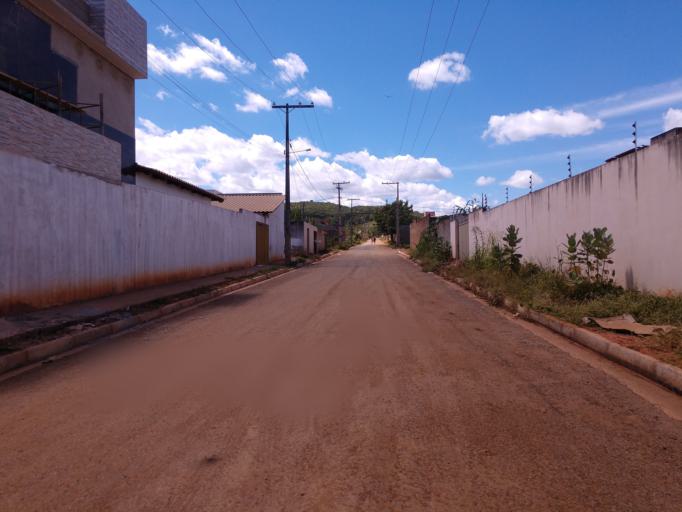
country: BR
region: Bahia
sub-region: Sao Desiderio
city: Sao Desiderio
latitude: -12.3579
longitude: -44.9735
